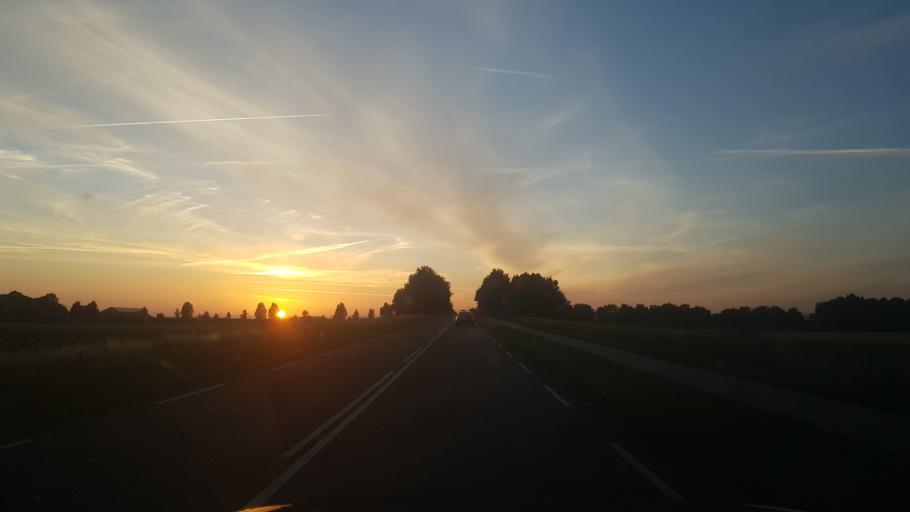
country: NL
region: Flevoland
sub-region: Gemeente Noordoostpolder
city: Emmeloord
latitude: 52.6936
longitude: 5.7301
